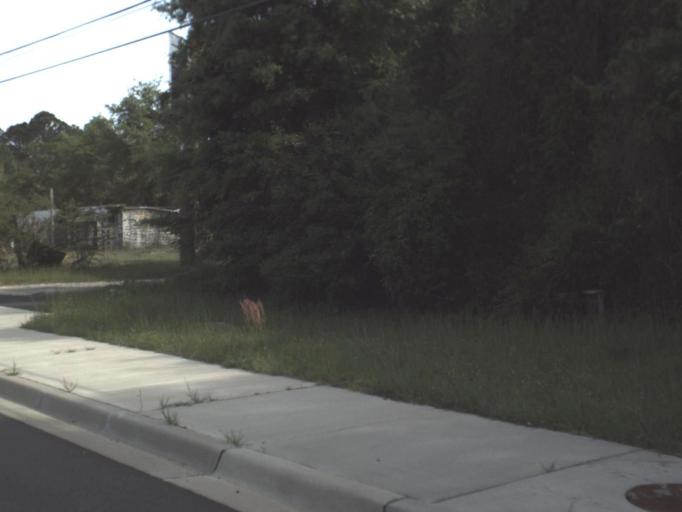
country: US
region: Florida
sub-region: Santa Rosa County
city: Holley
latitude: 30.4507
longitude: -86.9061
